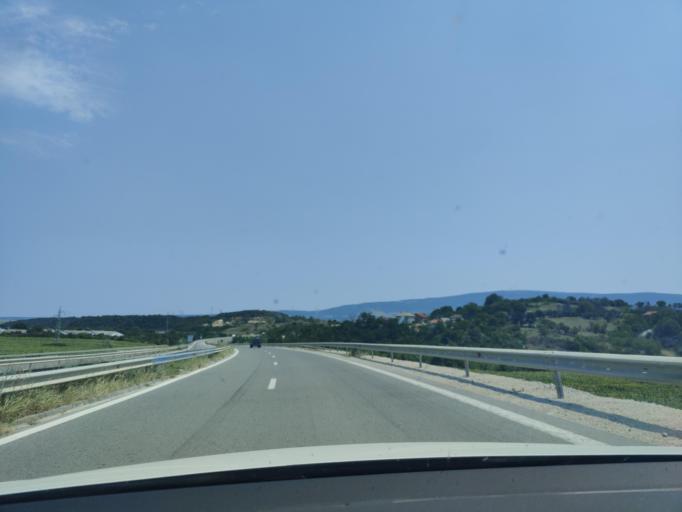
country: BG
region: Montana
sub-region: Obshtina Montana
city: Montana
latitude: 43.4401
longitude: 23.2191
